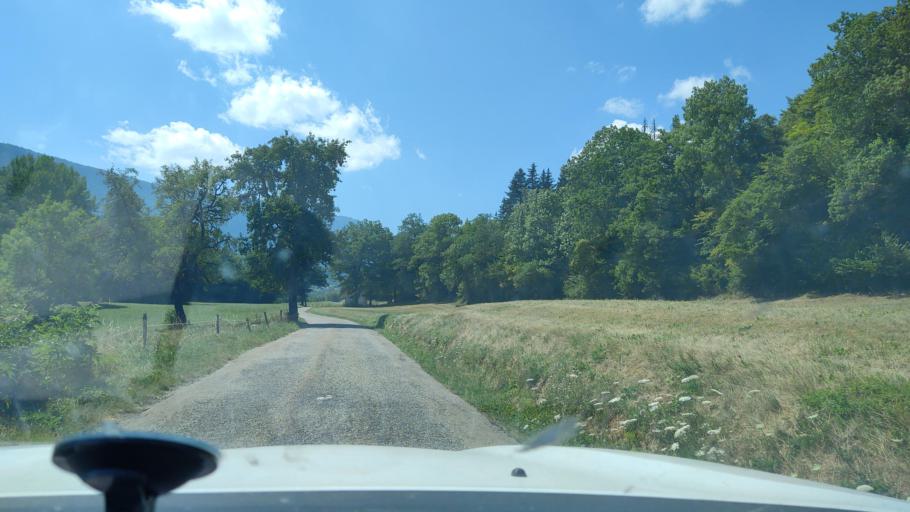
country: FR
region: Rhone-Alpes
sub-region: Departement de la Haute-Savoie
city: Cusy
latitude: 45.7047
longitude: 6.0796
